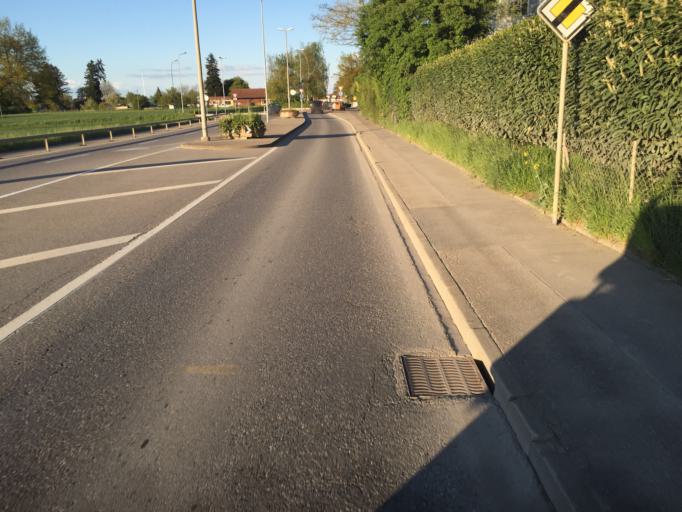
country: CH
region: Geneva
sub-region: Geneva
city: Bernex
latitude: 46.1775
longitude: 6.0710
